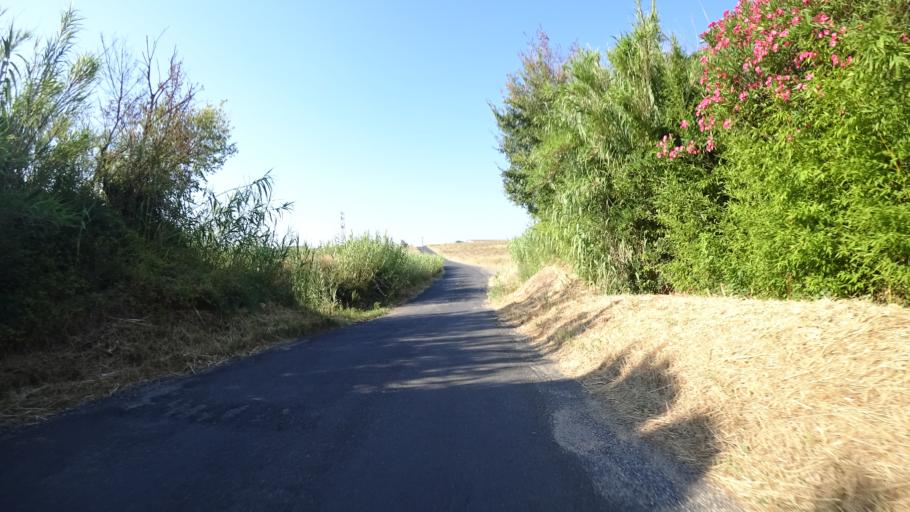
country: FR
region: Languedoc-Roussillon
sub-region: Departement des Pyrenees-Orientales
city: Cabestany
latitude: 42.6905
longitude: 2.9690
